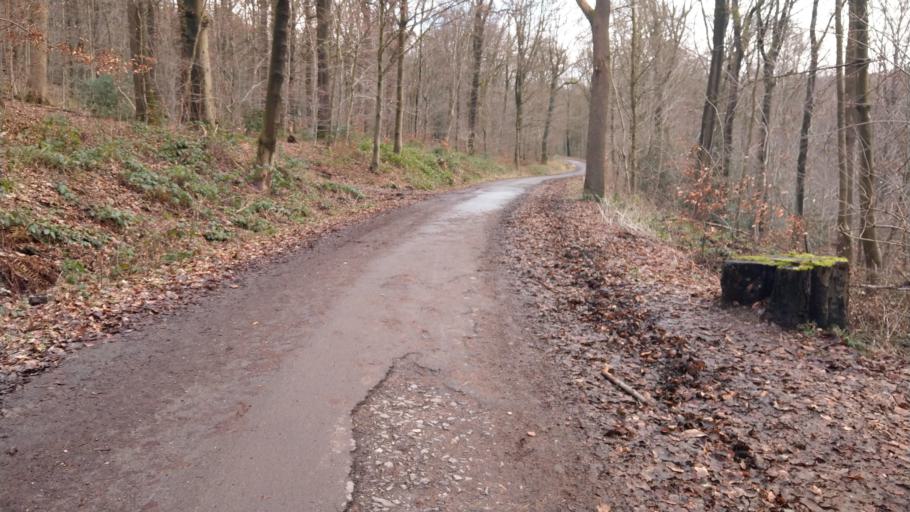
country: DE
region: North Rhine-Westphalia
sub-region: Regierungsbezirk Koln
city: Aachen
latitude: 50.7371
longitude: 6.0650
